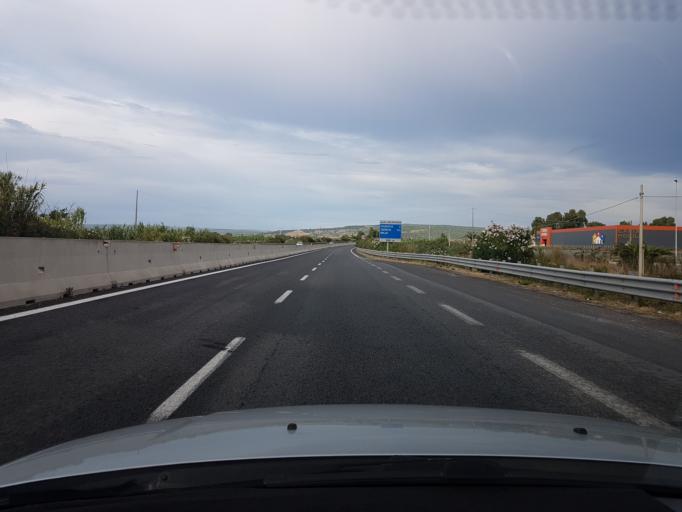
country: IT
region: Sardinia
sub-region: Provincia di Oristano
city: Tramatza
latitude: 39.9907
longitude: 8.6432
